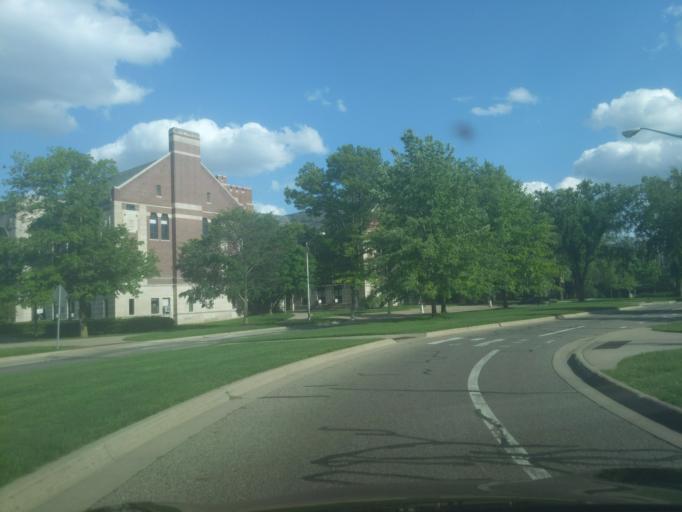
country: US
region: Michigan
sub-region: Ingham County
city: East Lansing
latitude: 42.7305
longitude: -84.4798
